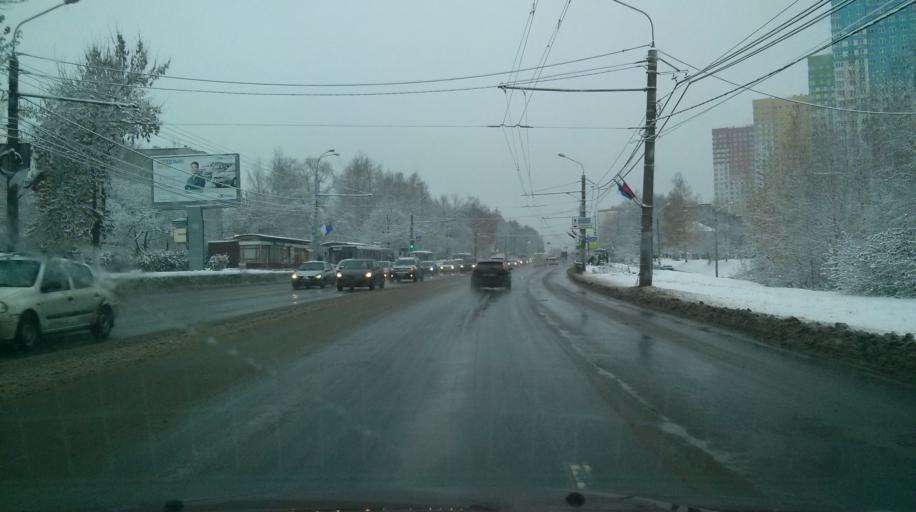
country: RU
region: Nizjnij Novgorod
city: Nizhniy Novgorod
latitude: 56.2411
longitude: 43.9627
